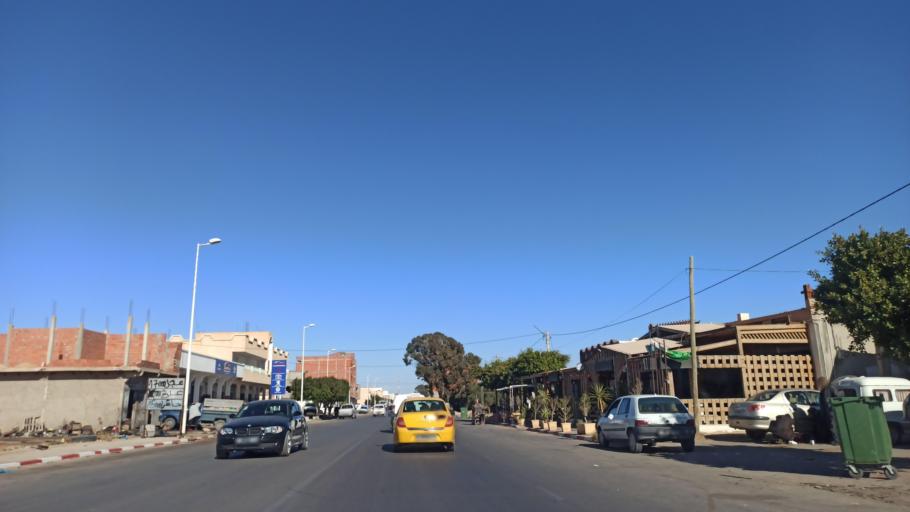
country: TN
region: Sidi Bu Zayd
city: Bi'r al Hufayy
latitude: 34.9189
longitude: 9.1866
